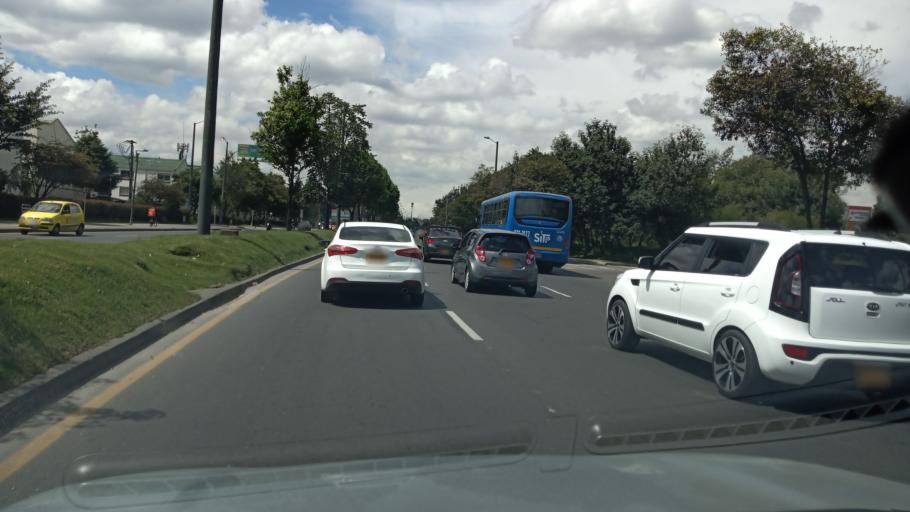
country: CO
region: Bogota D.C.
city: Bogota
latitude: 4.6739
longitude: -74.1239
